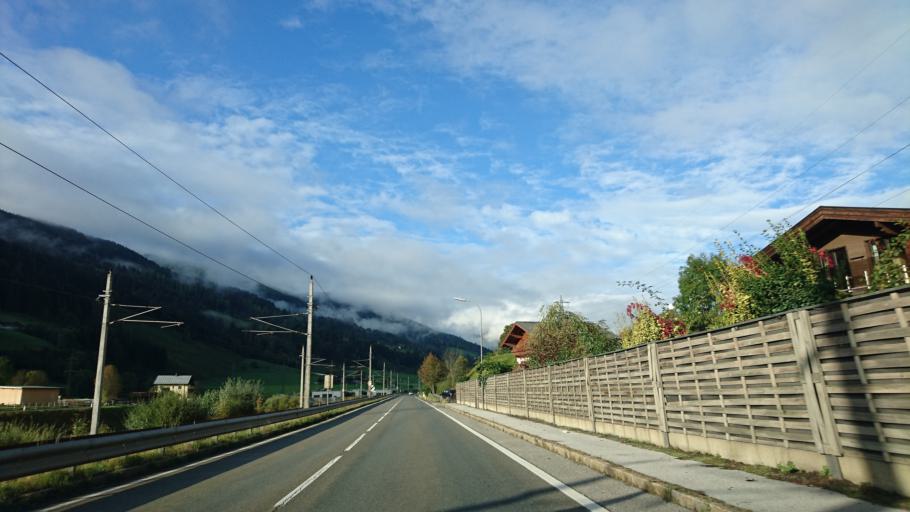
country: AT
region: Salzburg
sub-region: Politischer Bezirk Zell am See
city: Bruck an der Grossglocknerstrasse
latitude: 47.2879
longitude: 12.8847
